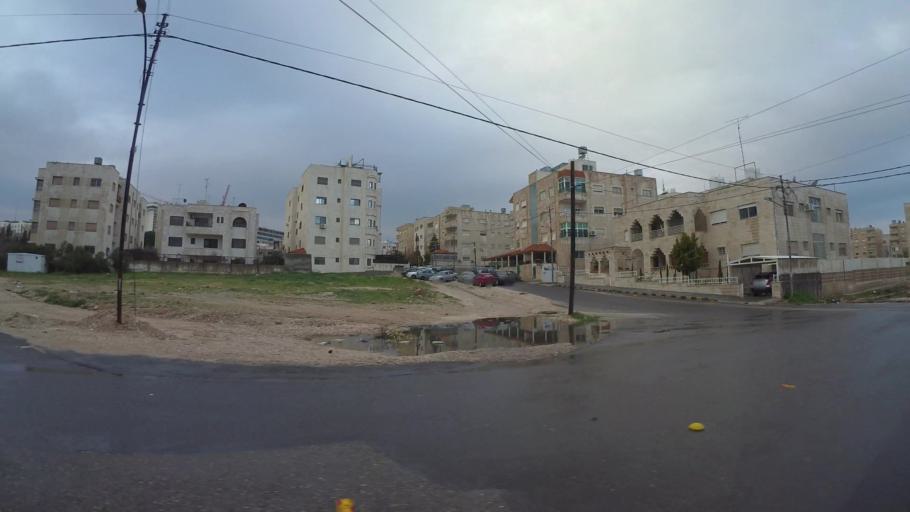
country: JO
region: Amman
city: Amman
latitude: 31.9773
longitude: 35.9117
